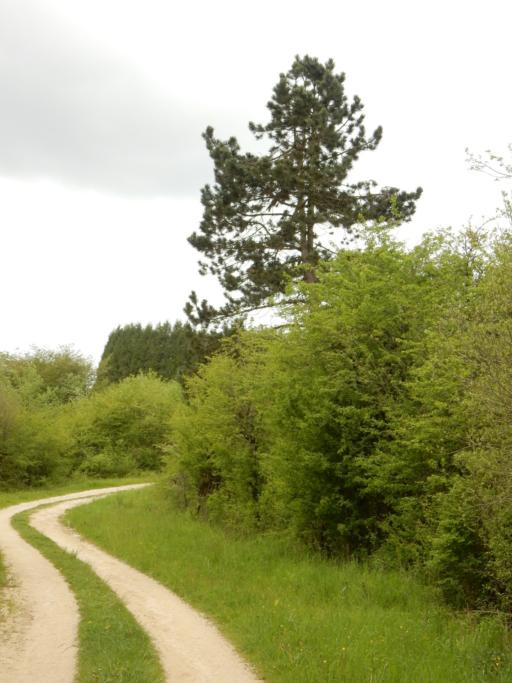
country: FR
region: Lorraine
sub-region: Departement de la Meuse
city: Verdun
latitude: 49.2054
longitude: 5.4291
